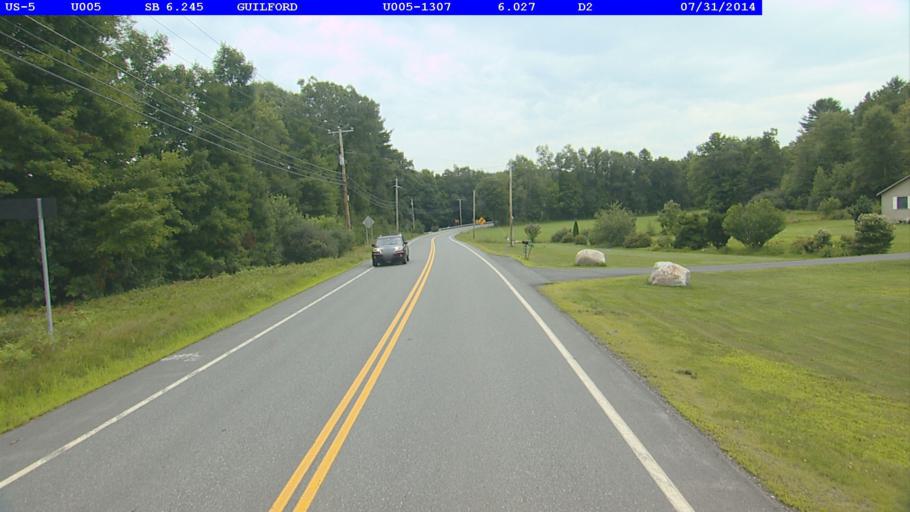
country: US
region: Vermont
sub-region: Windham County
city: Brattleboro
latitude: 42.8152
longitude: -72.5723
